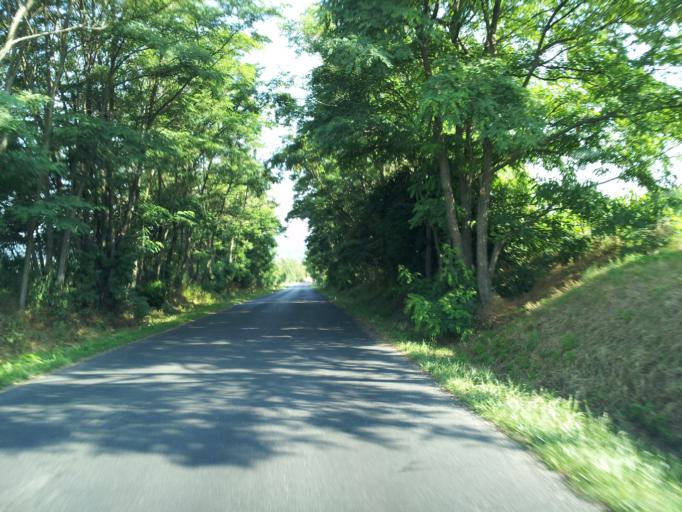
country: HU
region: Zala
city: Gyenesdias
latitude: 46.8593
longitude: 17.2998
